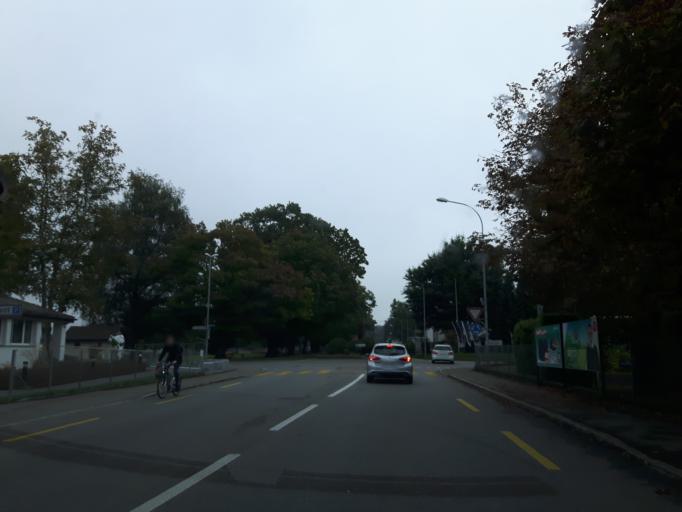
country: CH
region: Bern
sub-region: Oberaargau
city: Langenthal
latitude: 47.2198
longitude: 7.7836
